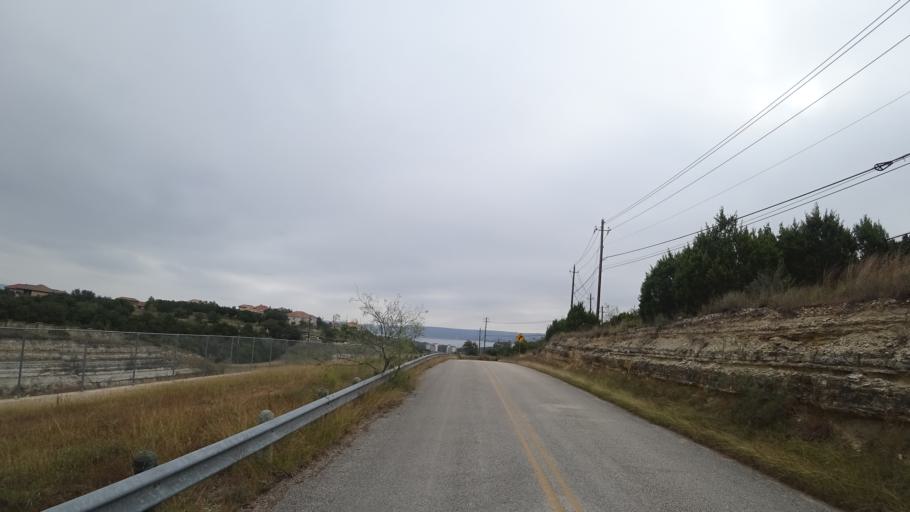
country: US
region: Texas
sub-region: Travis County
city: Hudson Bend
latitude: 30.3964
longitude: -97.9197
